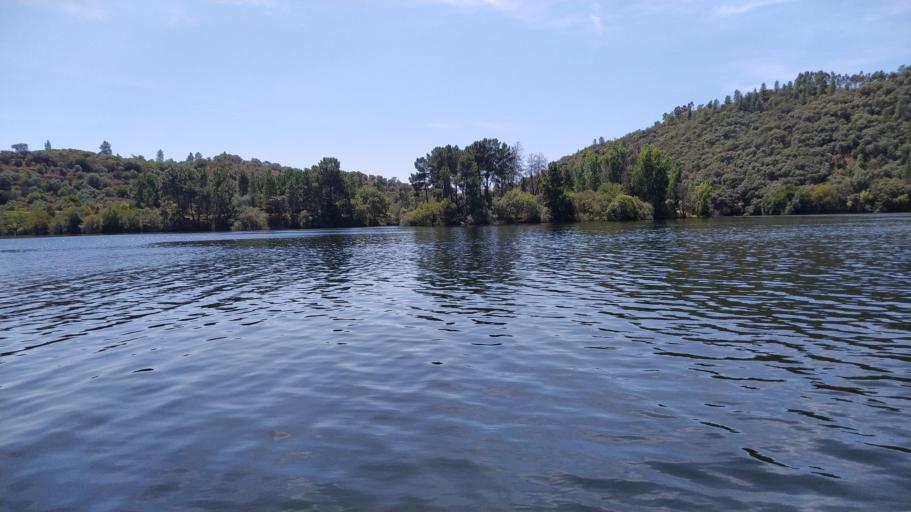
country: PT
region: Portalegre
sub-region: Nisa
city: Nisa
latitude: 39.6389
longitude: -7.6982
